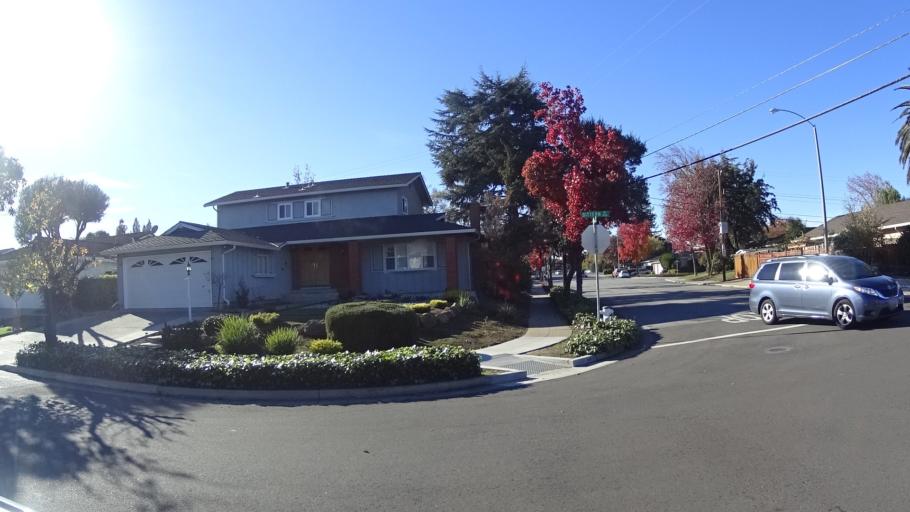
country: US
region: California
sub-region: Santa Clara County
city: Cupertino
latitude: 37.3429
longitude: -122.0303
